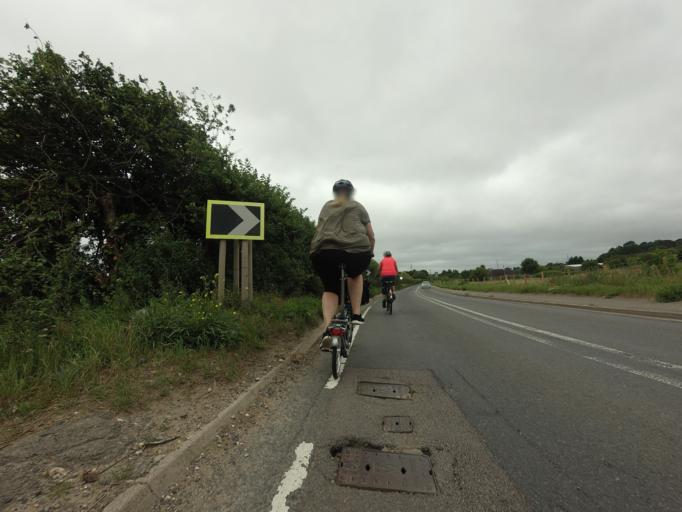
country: GB
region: England
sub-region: Kent
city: Longfield
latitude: 51.4104
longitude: 0.2823
